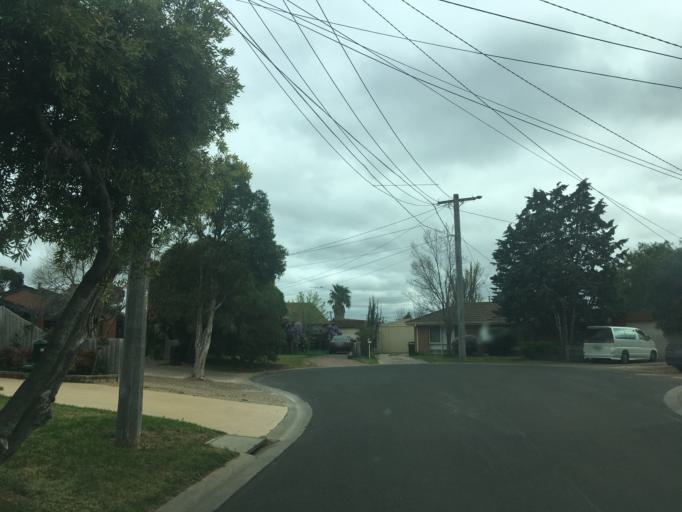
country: AU
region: Victoria
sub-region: Wyndham
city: Hoppers Crossing
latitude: -37.8665
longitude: 144.7094
